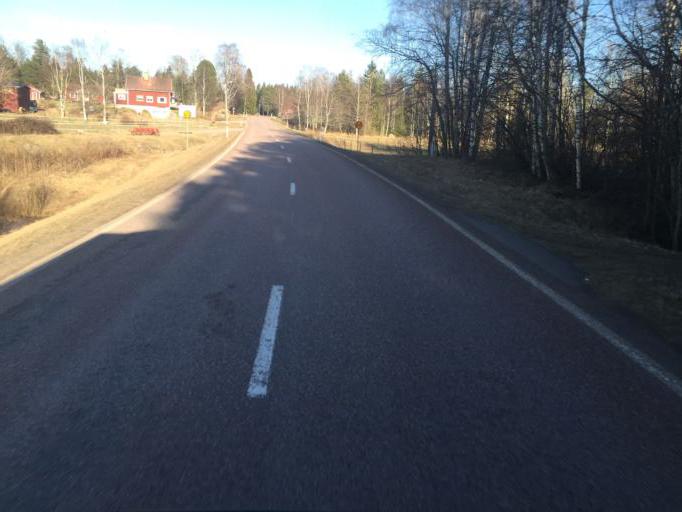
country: SE
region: Dalarna
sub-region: Vansbro Kommun
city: Jarna
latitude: 60.4454
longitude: 14.5247
